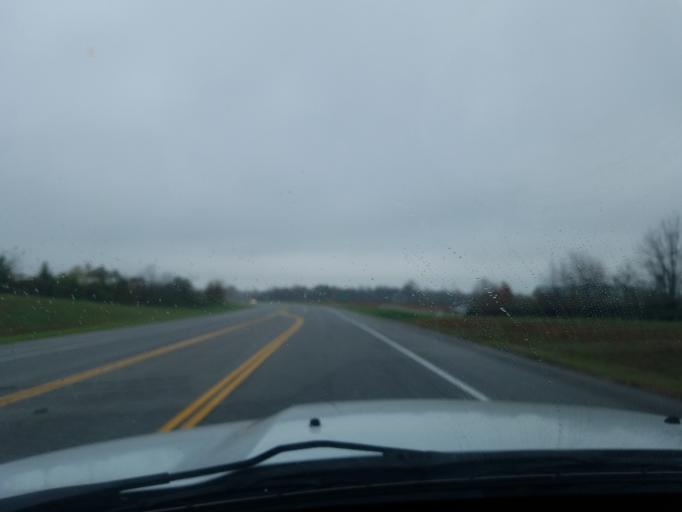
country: US
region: Kentucky
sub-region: Larue County
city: Hodgenville
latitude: 37.5513
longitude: -85.7306
